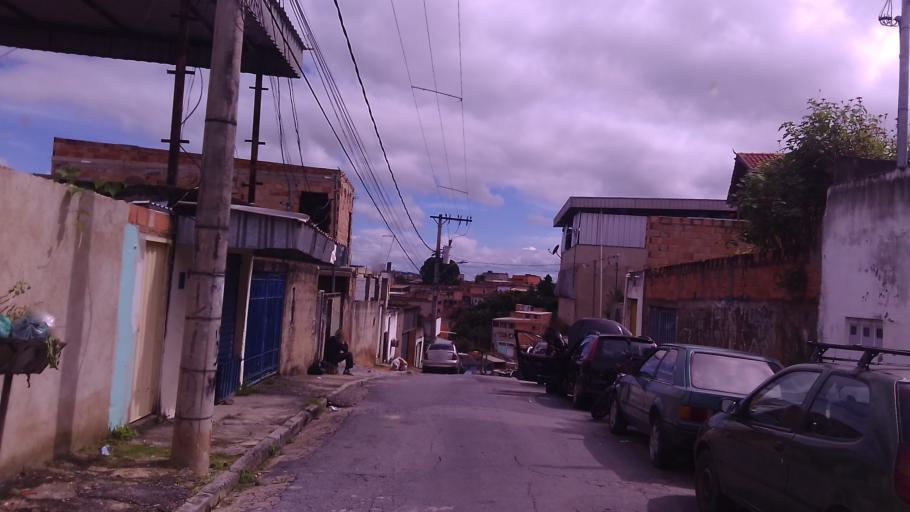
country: BR
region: Minas Gerais
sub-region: Santa Luzia
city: Santa Luzia
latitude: -19.8349
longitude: -43.8929
